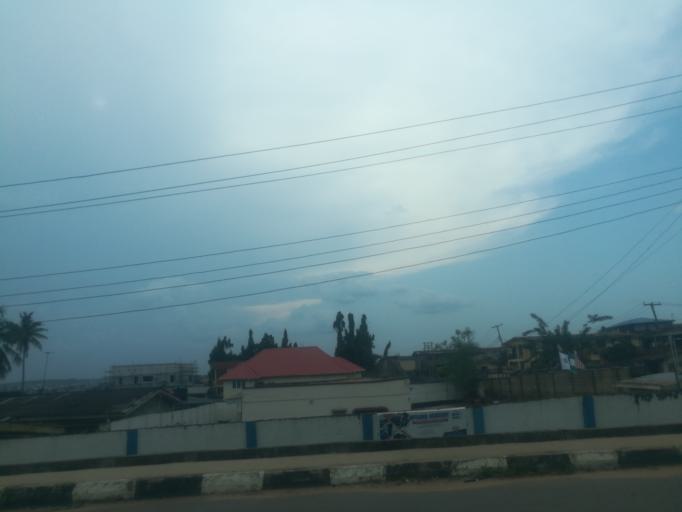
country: NG
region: Oyo
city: Ibadan
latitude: 7.3776
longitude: 3.8288
